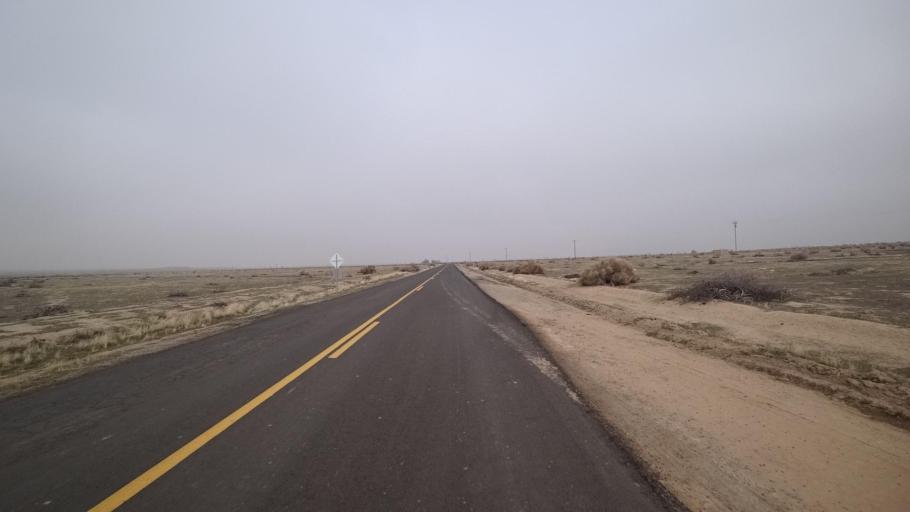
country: US
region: California
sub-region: Kern County
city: Maricopa
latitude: 35.0623
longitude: -119.3507
